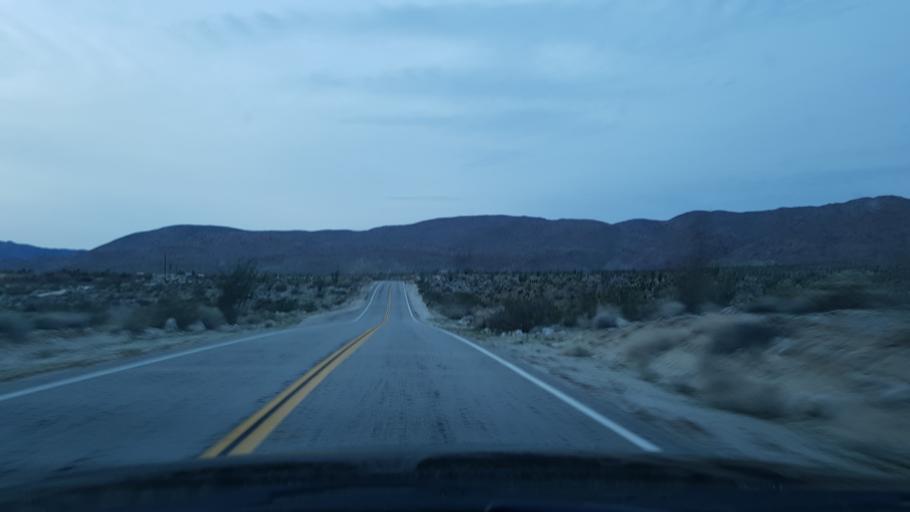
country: US
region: California
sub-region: San Diego County
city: Pine Valley
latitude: 32.9735
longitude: -116.3433
